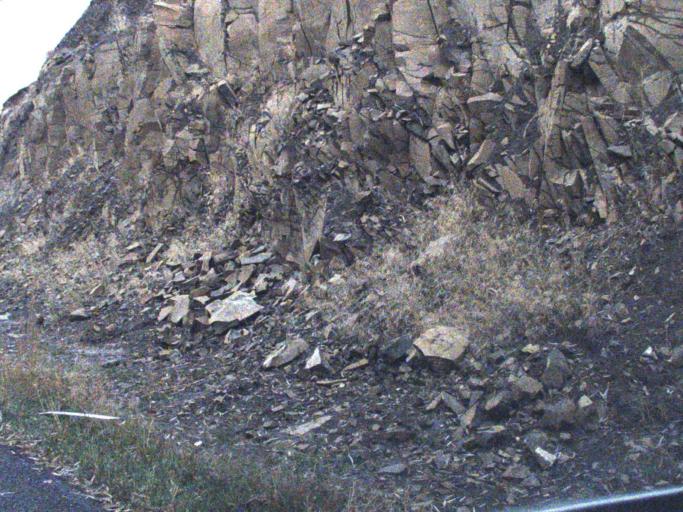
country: US
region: Washington
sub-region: Walla Walla County
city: Waitsburg
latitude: 46.5276
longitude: -118.1403
